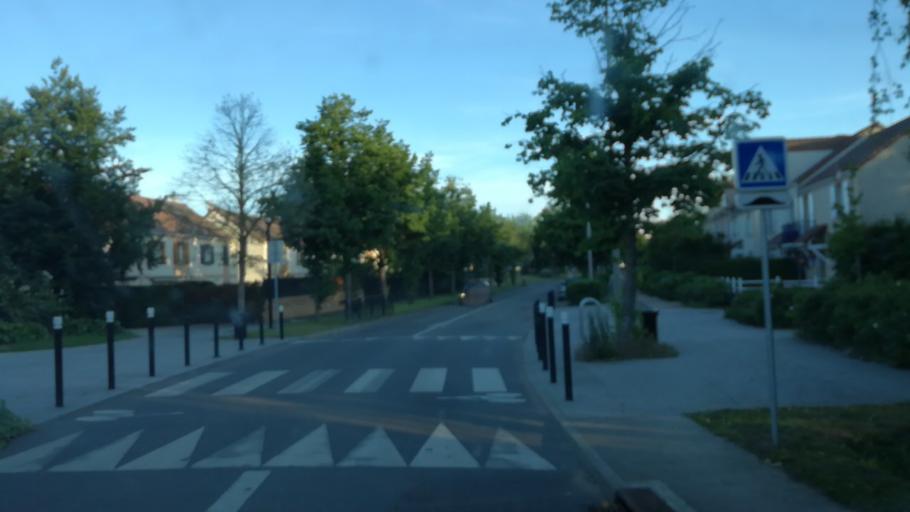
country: FR
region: Ile-de-France
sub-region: Departement des Yvelines
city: Elancourt
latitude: 48.7705
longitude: 1.9623
